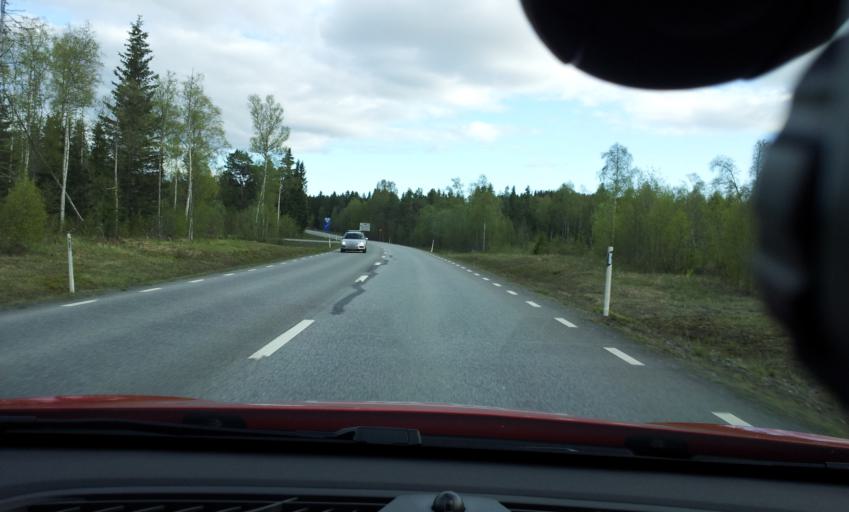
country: SE
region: Jaemtland
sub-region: OEstersunds Kommun
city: Ostersund
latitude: 63.1797
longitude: 14.5341
